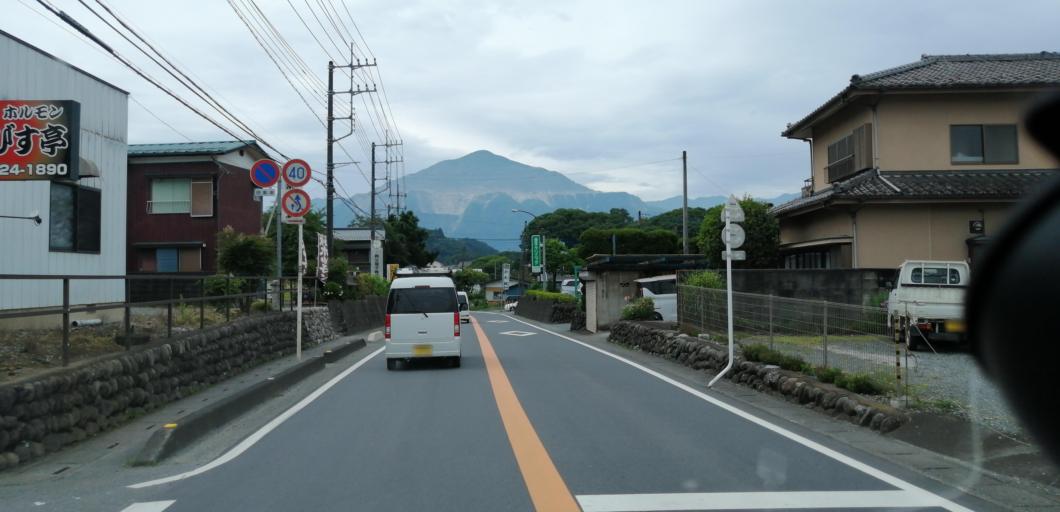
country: JP
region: Saitama
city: Chichibu
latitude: 36.0150
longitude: 139.1123
